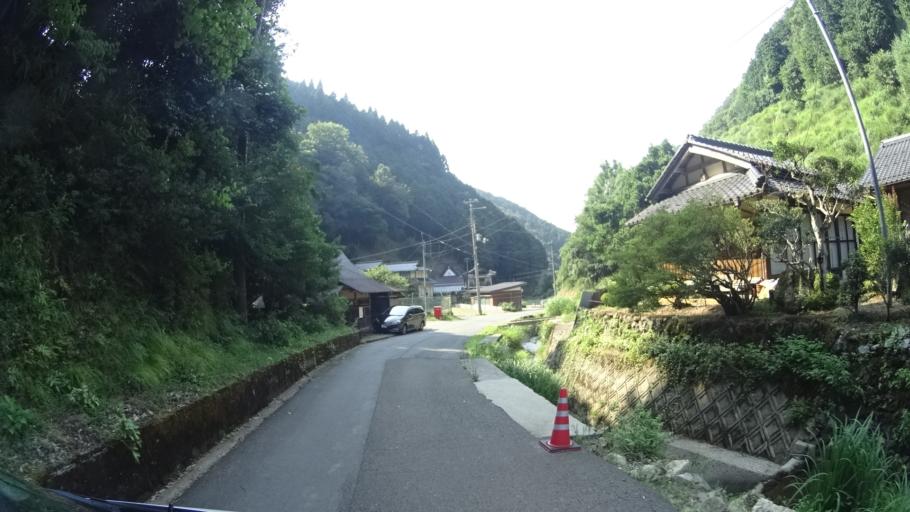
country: JP
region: Kyoto
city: Ayabe
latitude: 35.4011
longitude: 135.2438
